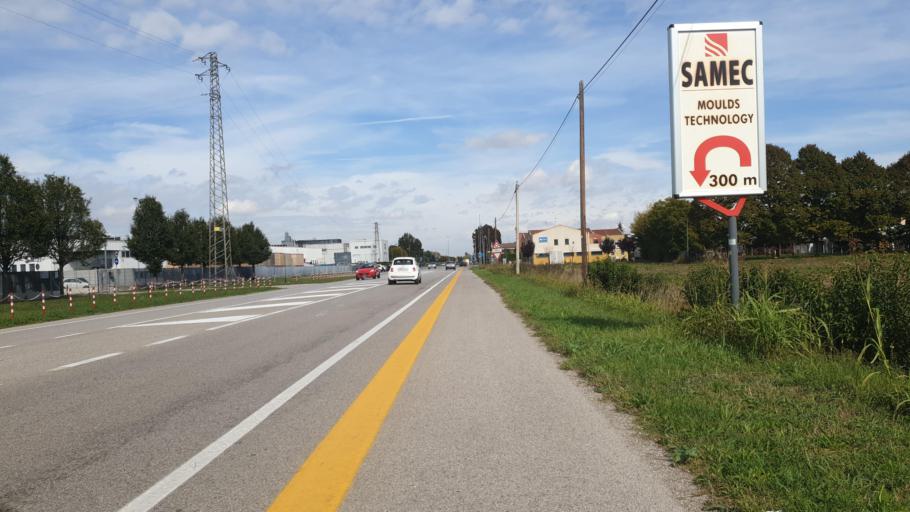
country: IT
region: Veneto
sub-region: Provincia di Padova
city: Arzergrande
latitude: 45.2843
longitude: 12.0543
